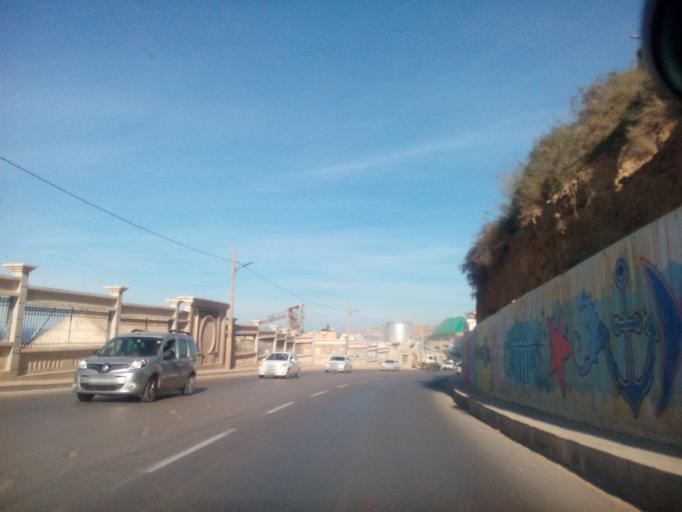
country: DZ
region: Mostaganem
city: Mostaganem
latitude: 35.9355
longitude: 0.0804
